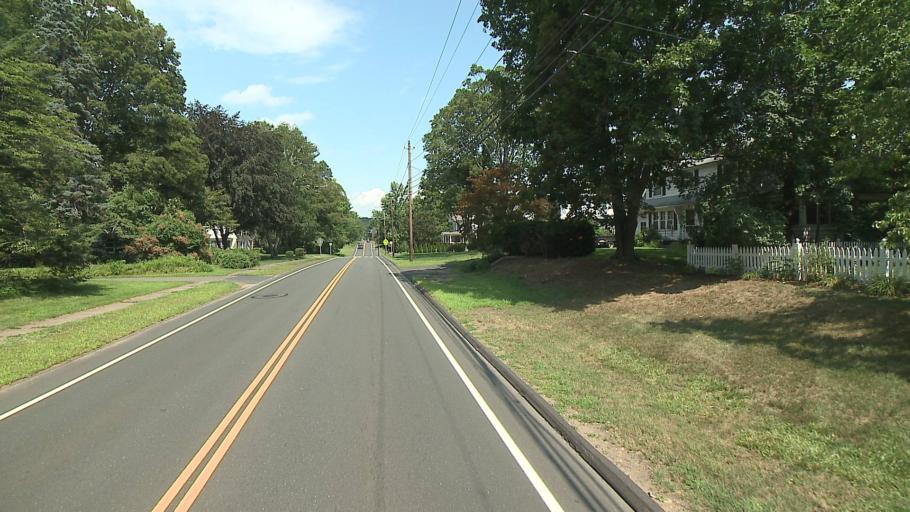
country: US
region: Connecticut
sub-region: Hartford County
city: Collinsville
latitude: 41.7619
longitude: -72.8882
